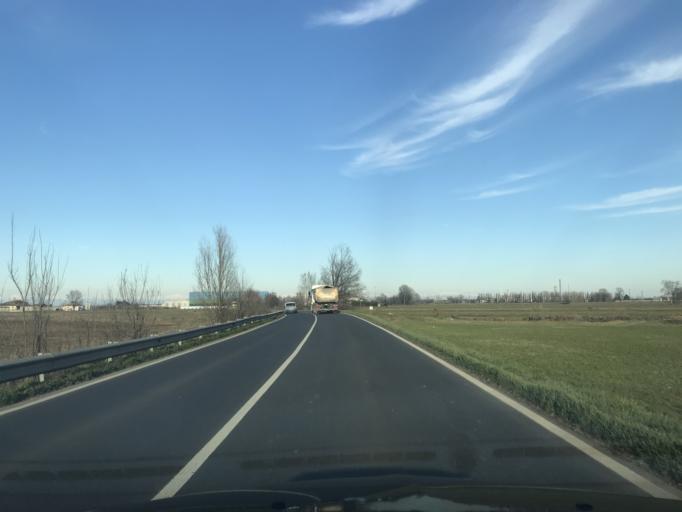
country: IT
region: Lombardy
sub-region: Provincia di Lodi
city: Borgo San Giovanni
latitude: 45.2637
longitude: 9.4367
